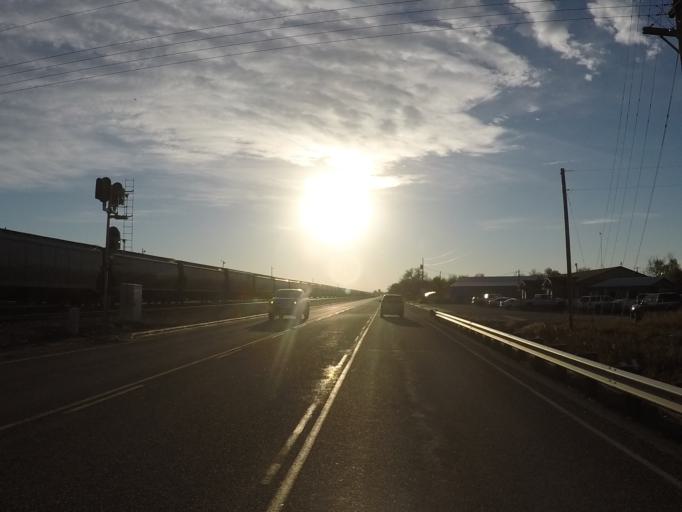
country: US
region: Montana
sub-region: Yellowstone County
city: Laurel
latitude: 45.6753
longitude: -108.7460
